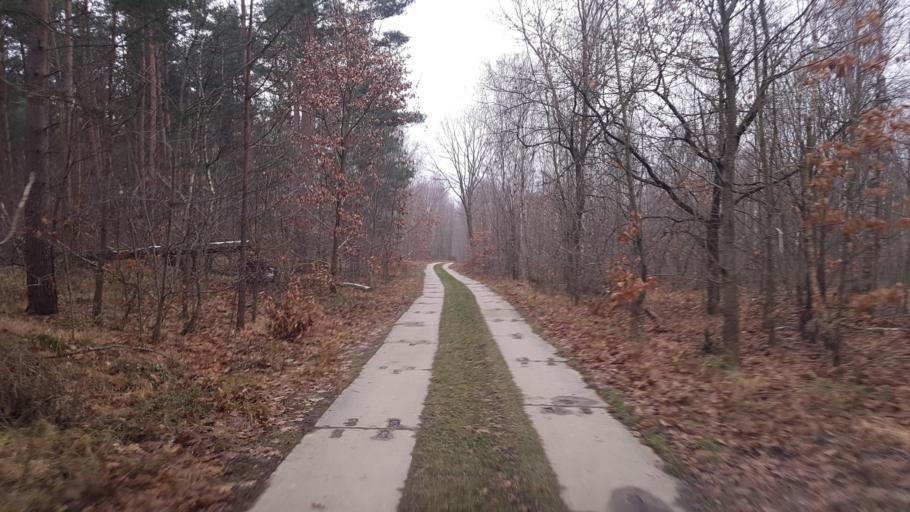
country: DE
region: Brandenburg
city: Plessa
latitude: 51.4963
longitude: 13.6384
